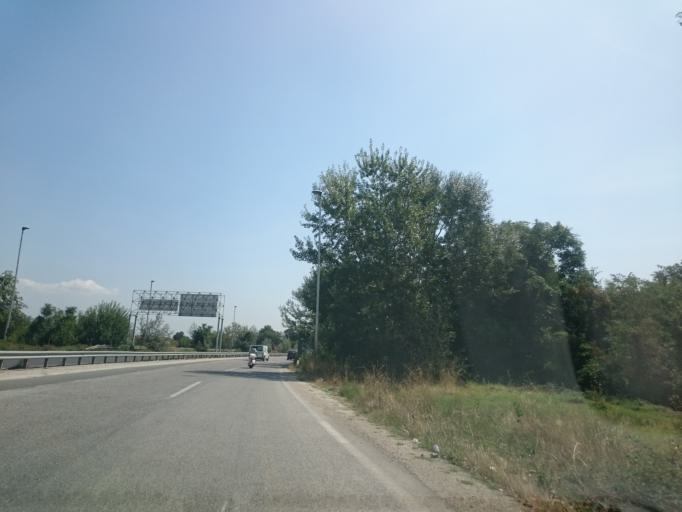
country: MK
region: Saraj
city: Saraj
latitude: 42.0086
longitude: 21.3265
